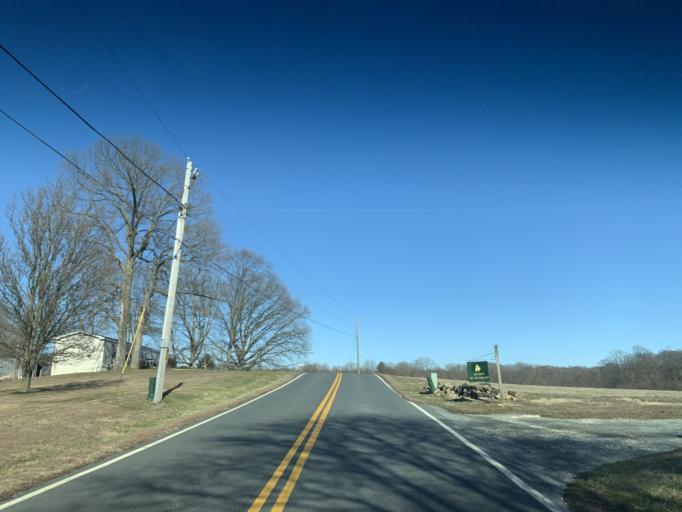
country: US
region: Maryland
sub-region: Cecil County
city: Rising Sun
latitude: 39.6667
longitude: -76.1307
